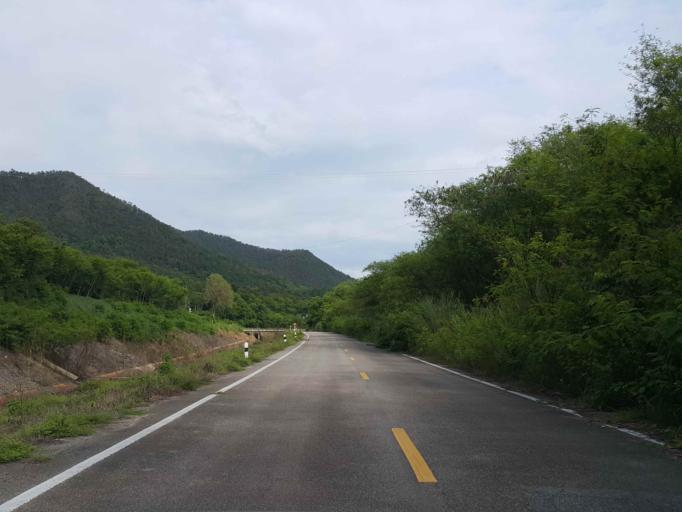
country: TH
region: Chiang Mai
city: San Sai
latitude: 18.9359
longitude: 99.1393
